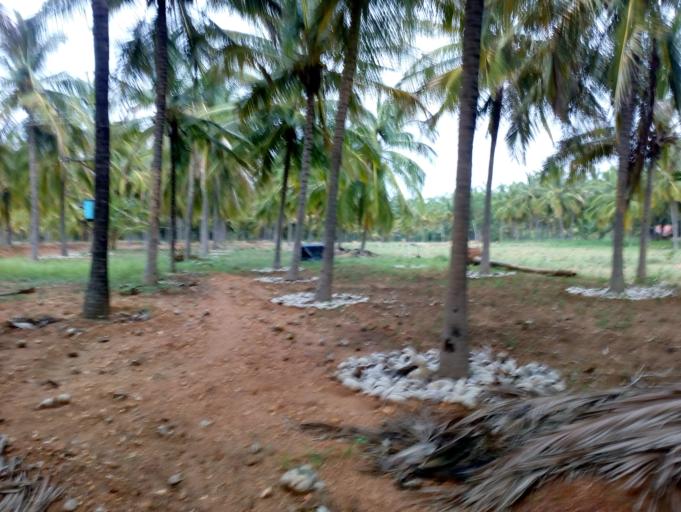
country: IN
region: Karnataka
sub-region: Tumkur
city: Turuvekere
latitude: 13.1912
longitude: 76.7152
